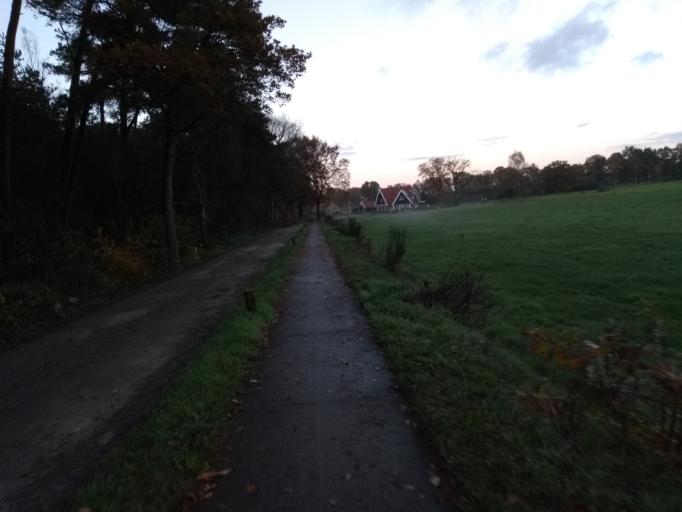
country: NL
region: Overijssel
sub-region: Gemeente Borne
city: Borne
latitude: 52.3611
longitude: 6.7261
